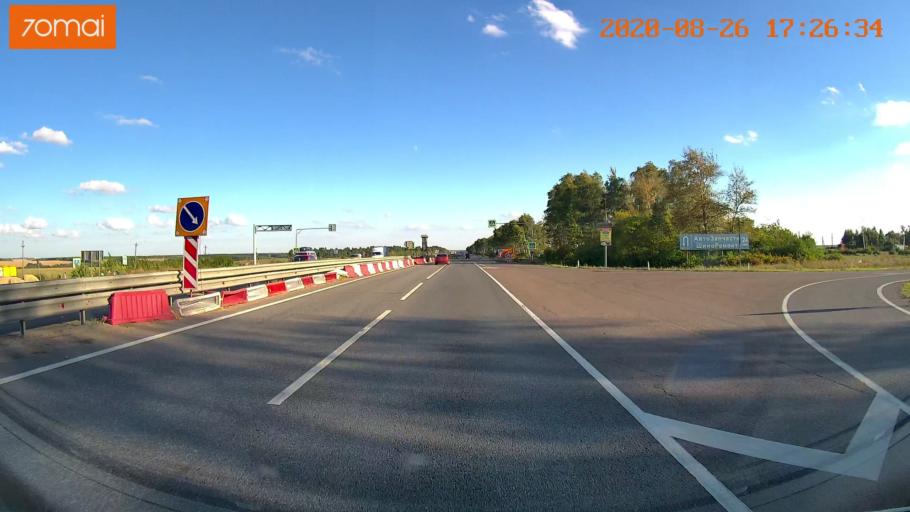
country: RU
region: Tula
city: Kazachka
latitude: 53.4848
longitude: 38.1181
